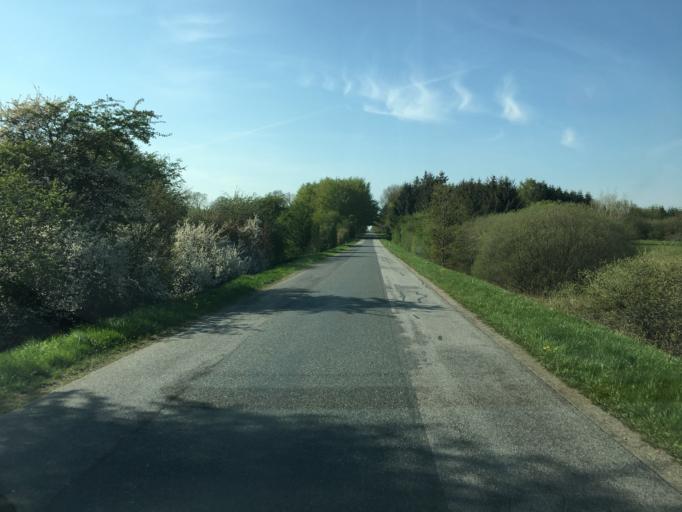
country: DK
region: South Denmark
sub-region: Haderslev Kommune
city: Vojens
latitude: 55.2382
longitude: 9.3246
